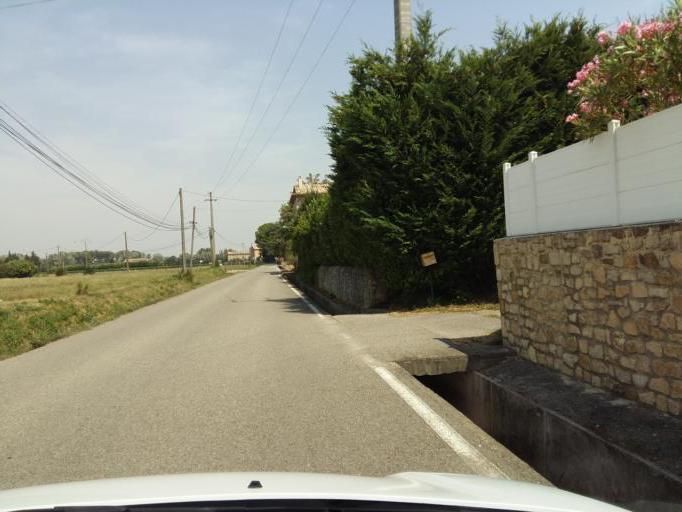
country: FR
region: Languedoc-Roussillon
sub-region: Departement du Gard
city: Pont-Saint-Esprit
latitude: 44.2627
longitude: 4.6640
